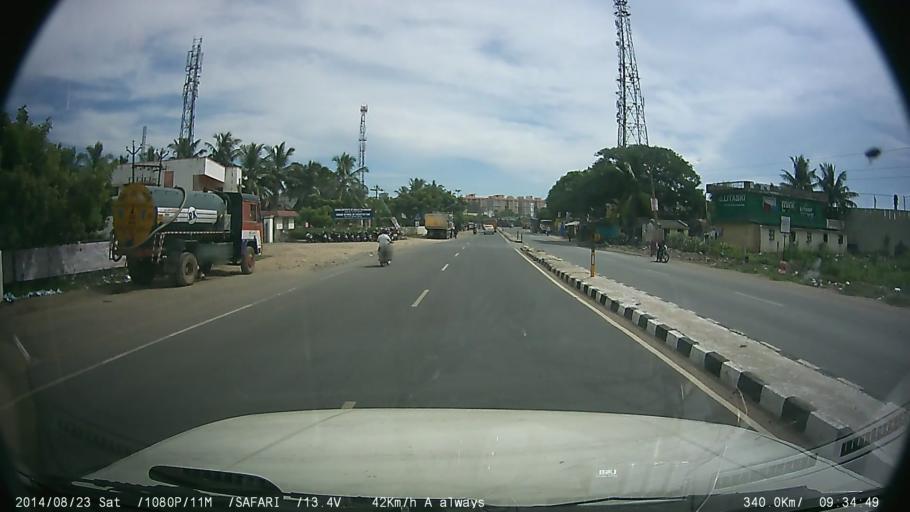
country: IN
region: Tamil Nadu
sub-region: Kancheepuram
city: Injambakkam
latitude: 12.8170
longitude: 80.2295
